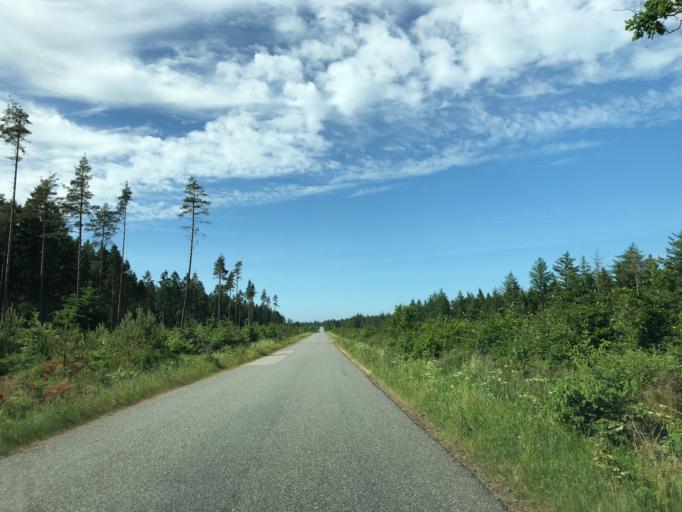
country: DK
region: Central Jutland
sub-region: Herning Kommune
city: Kibaek
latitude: 56.0521
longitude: 8.9261
